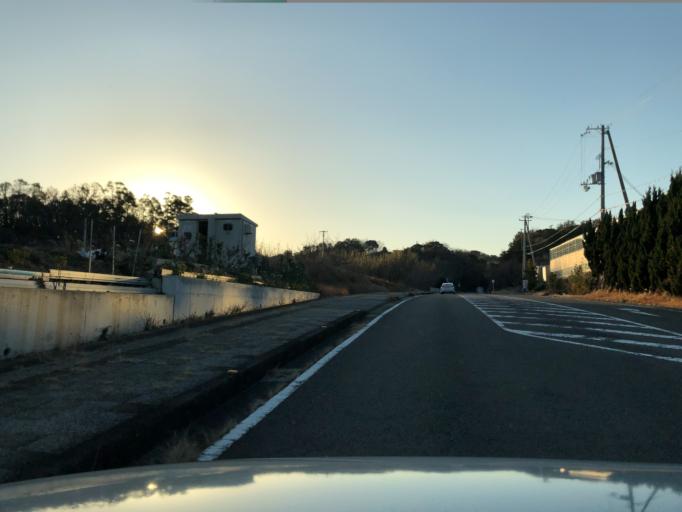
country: JP
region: Wakayama
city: Tanabe
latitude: 33.6612
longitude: 135.3786
